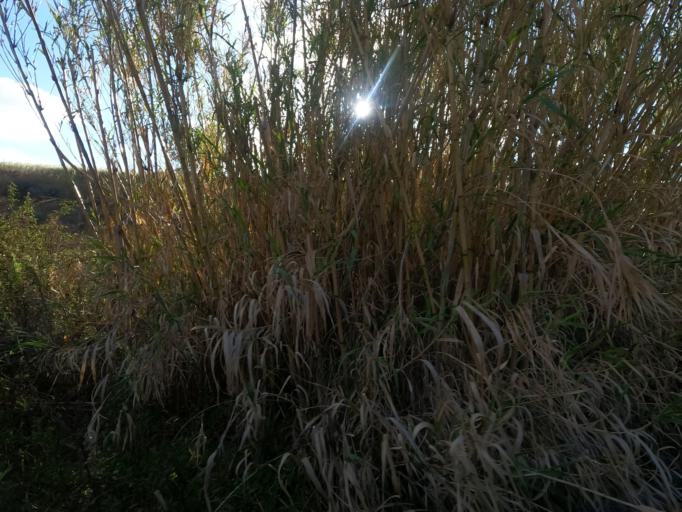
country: CY
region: Lefkosia
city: Peristerona
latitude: 35.0698
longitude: 33.0461
